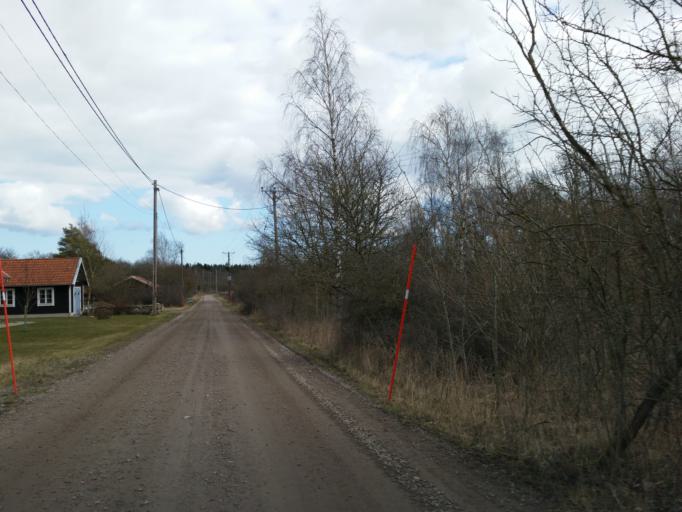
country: SE
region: Kalmar
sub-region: Morbylanga Kommun
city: Sodra Sandby
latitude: 56.6770
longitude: 16.6131
